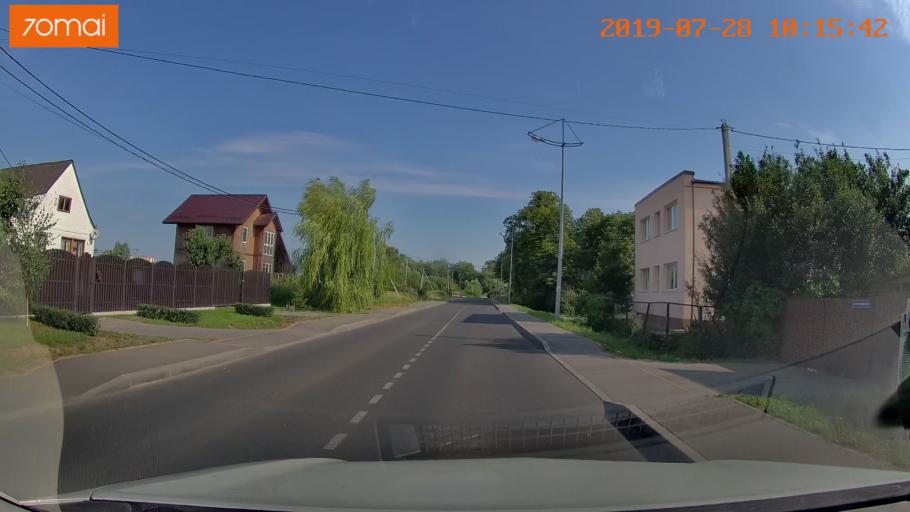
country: RU
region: Kaliningrad
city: Bol'shoe Isakovo
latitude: 54.7230
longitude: 20.6008
